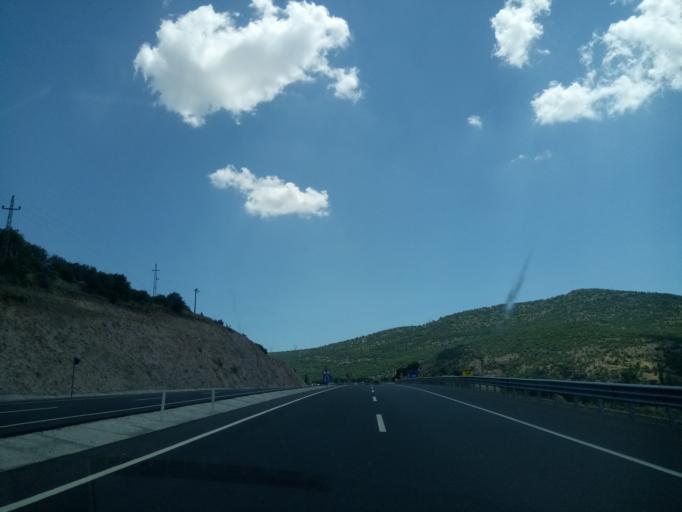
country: TR
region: Konya
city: Cavus
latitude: 37.6810
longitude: 32.0093
